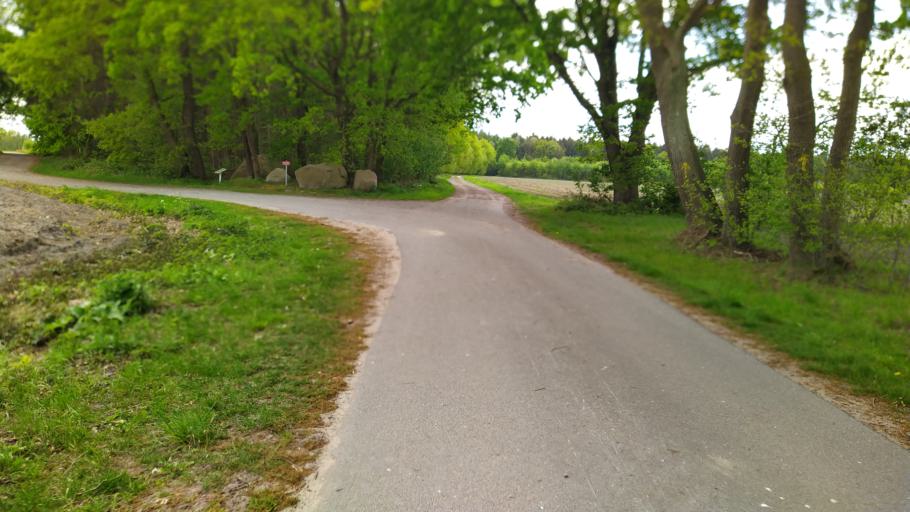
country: DE
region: Lower Saxony
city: Ahlerstedt
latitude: 53.3700
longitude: 9.3937
